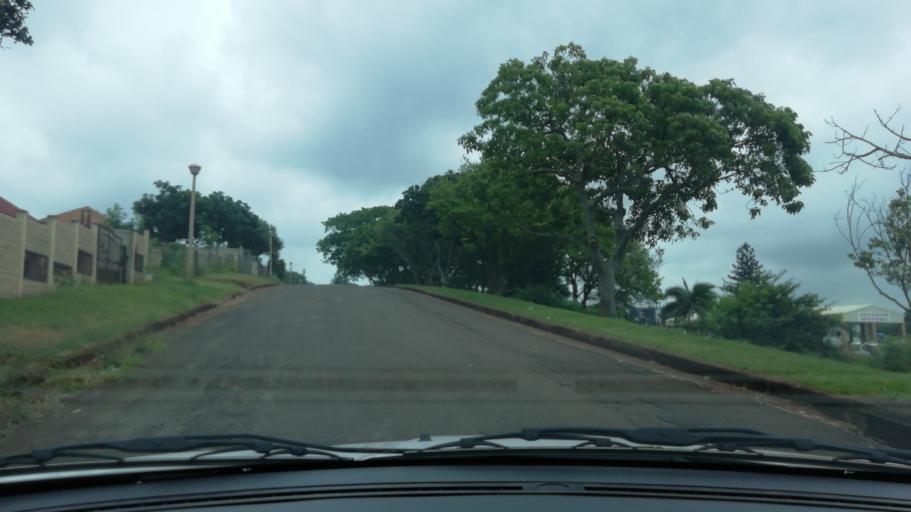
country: ZA
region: KwaZulu-Natal
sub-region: uThungulu District Municipality
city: Empangeni
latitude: -28.7621
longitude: 31.9049
